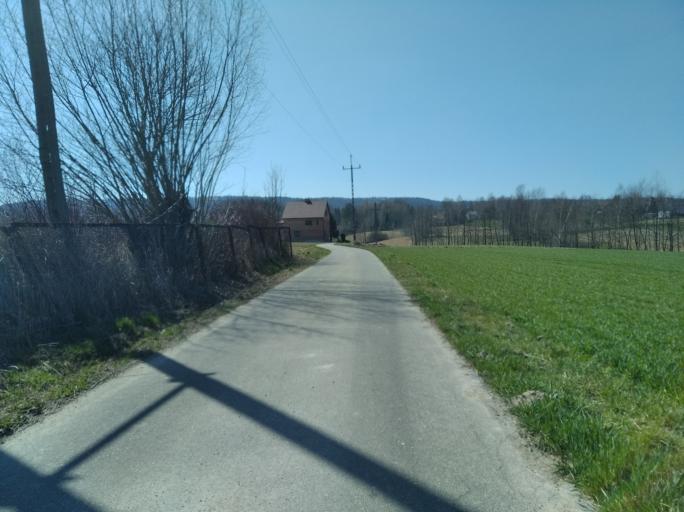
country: PL
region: Subcarpathian Voivodeship
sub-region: Powiat strzyzowski
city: Strzyzow
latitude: 49.8410
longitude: 21.8159
